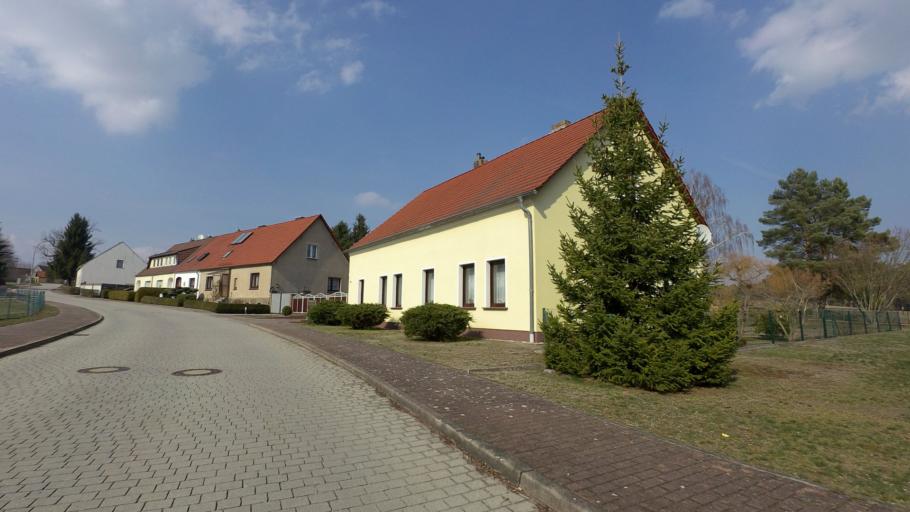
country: DE
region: Brandenburg
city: Dahme
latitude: 51.9398
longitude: 13.4461
